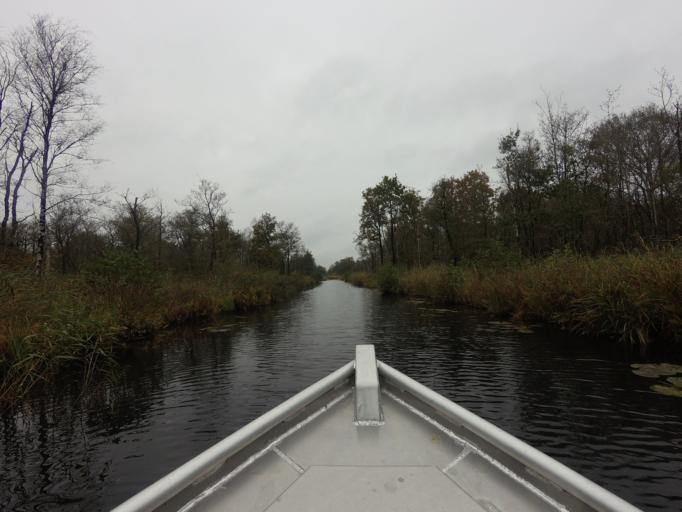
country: NL
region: Overijssel
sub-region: Gemeente Steenwijkerland
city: Oldemarkt
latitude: 52.7848
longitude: 5.9517
